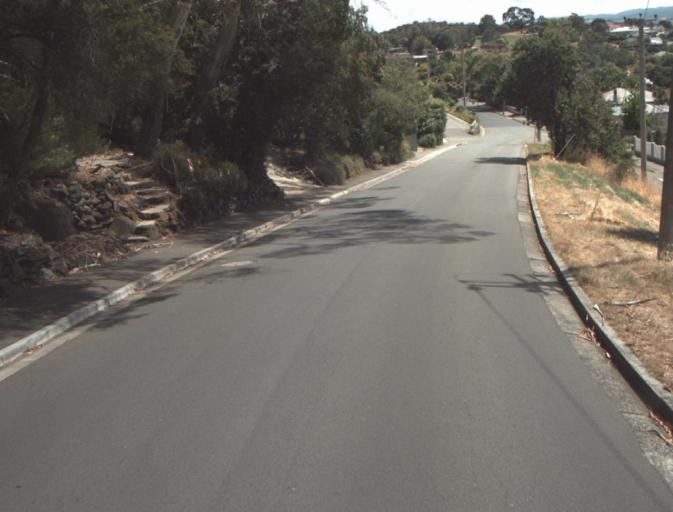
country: AU
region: Tasmania
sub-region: Launceston
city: West Launceston
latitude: -41.4543
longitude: 147.1316
